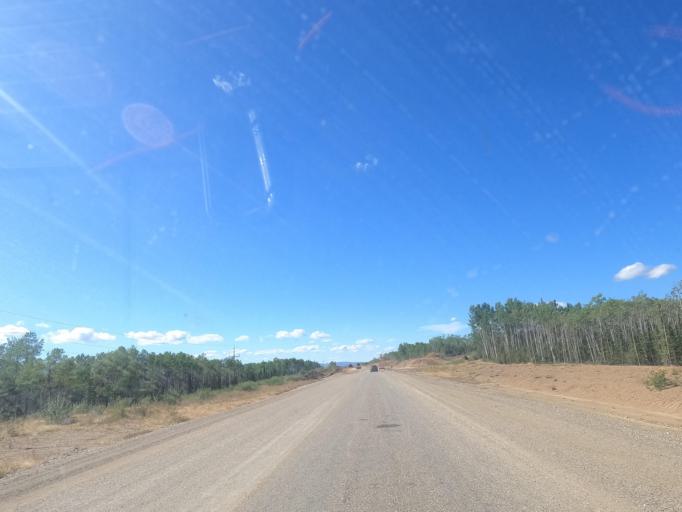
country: CA
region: Yukon
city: Dawson City
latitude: 63.8589
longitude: -138.0498
